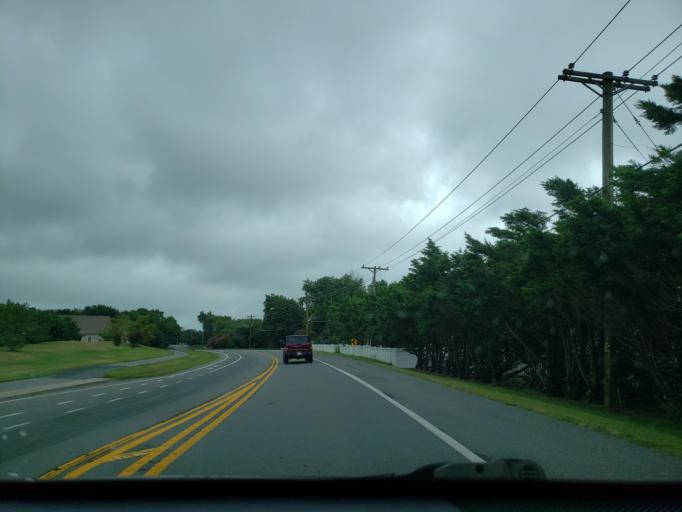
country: US
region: Delaware
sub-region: Sussex County
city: Milton
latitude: 38.7581
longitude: -75.2271
